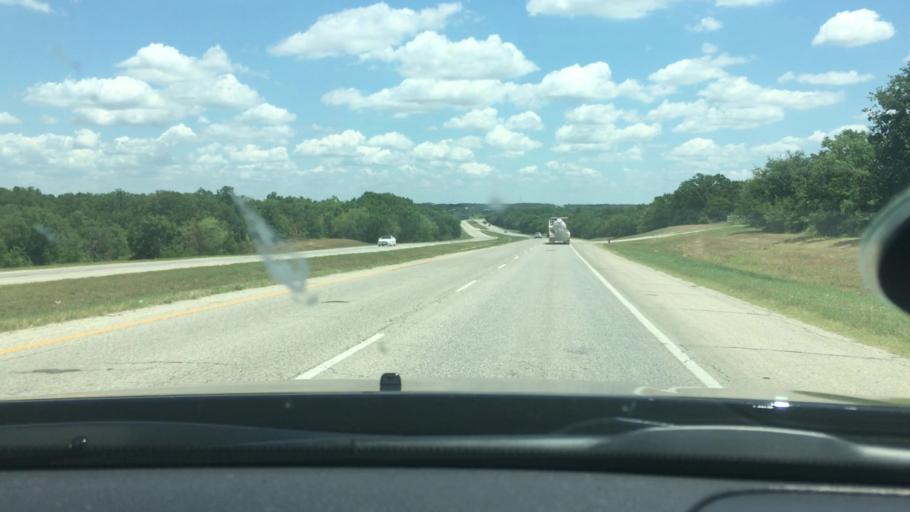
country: US
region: Oklahoma
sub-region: Carter County
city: Wilson
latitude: 34.1728
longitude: -97.3841
